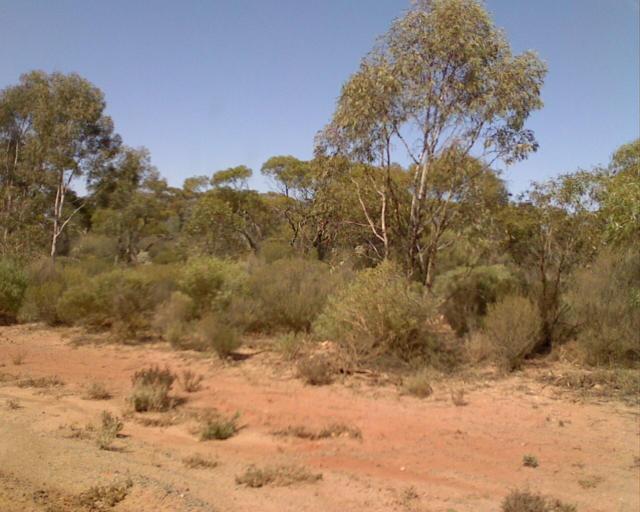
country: AU
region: Western Australia
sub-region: Kalgoorlie/Boulder
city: Boulder
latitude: -30.8273
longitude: 121.3800
